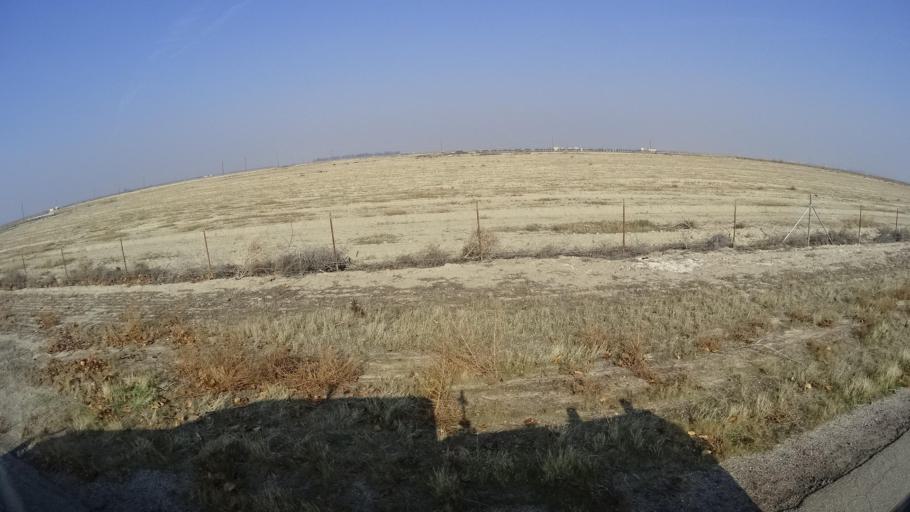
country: US
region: California
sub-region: Kern County
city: Buttonwillow
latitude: 35.3331
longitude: -119.3622
